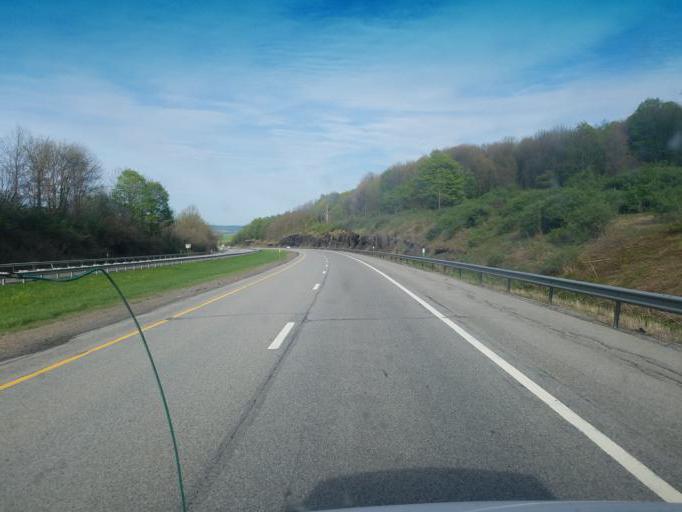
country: US
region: New York
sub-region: Herkimer County
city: Little Falls
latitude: 43.0100
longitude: -74.8402
